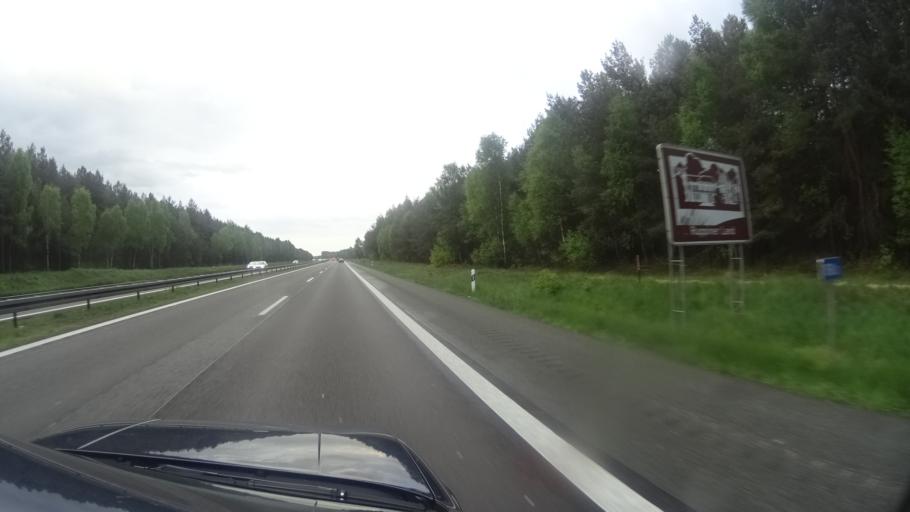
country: DE
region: Brandenburg
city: Walsleben
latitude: 53.0256
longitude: 12.5727
